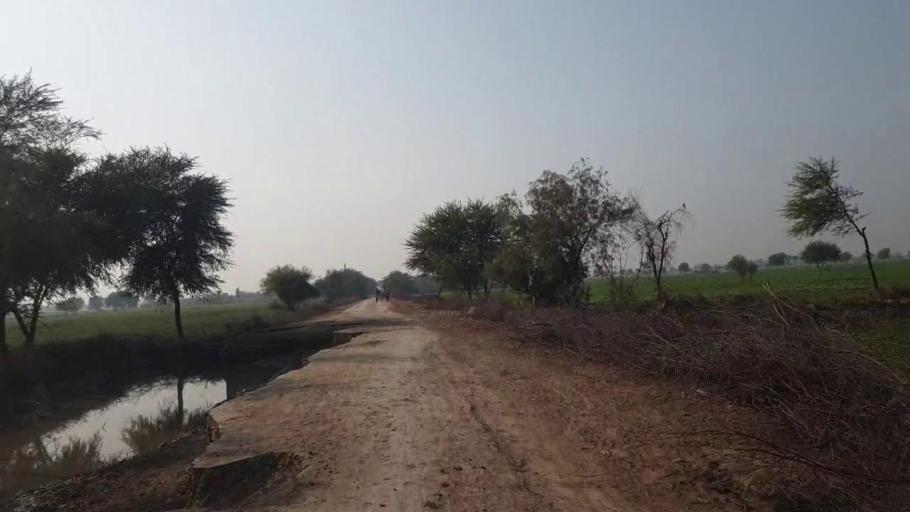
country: PK
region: Sindh
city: Shahdadpur
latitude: 26.0005
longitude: 68.5425
